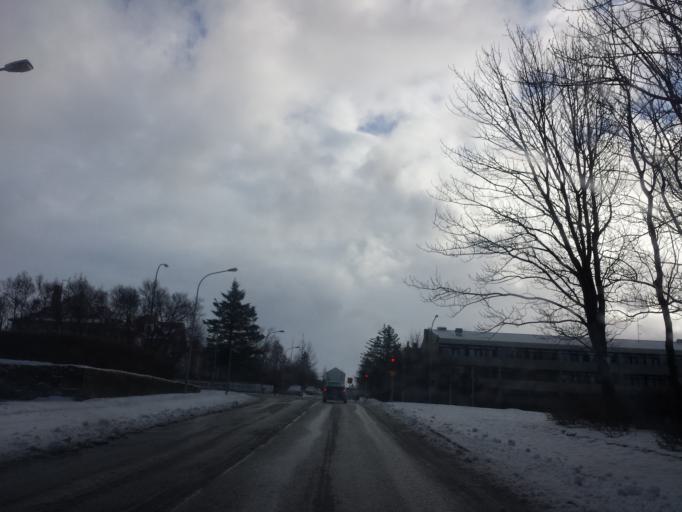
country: IS
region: Capital Region
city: Reykjavik
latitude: 64.1379
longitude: -21.9096
